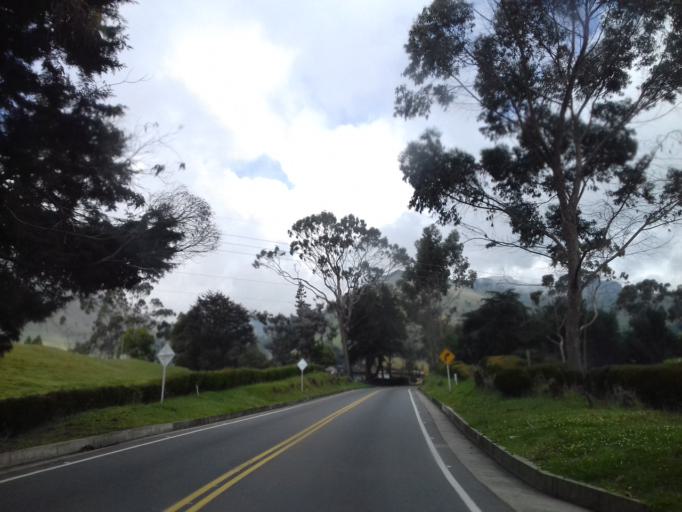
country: CO
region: Caldas
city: Villamaria
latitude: 5.0166
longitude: -75.3586
